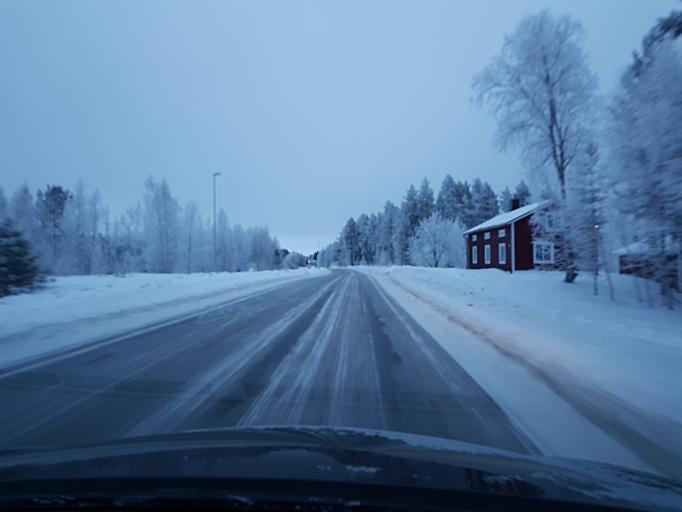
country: SE
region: Norrbotten
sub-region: Pitea Kommun
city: Roknas
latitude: 65.3486
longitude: 21.1071
